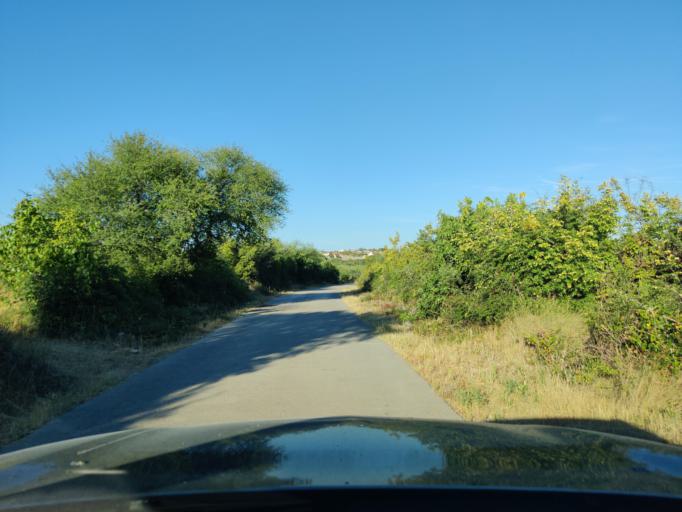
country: HR
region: Sibensko-Kniniska
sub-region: Grad Sibenik
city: Pirovac
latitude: 43.8625
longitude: 15.7093
